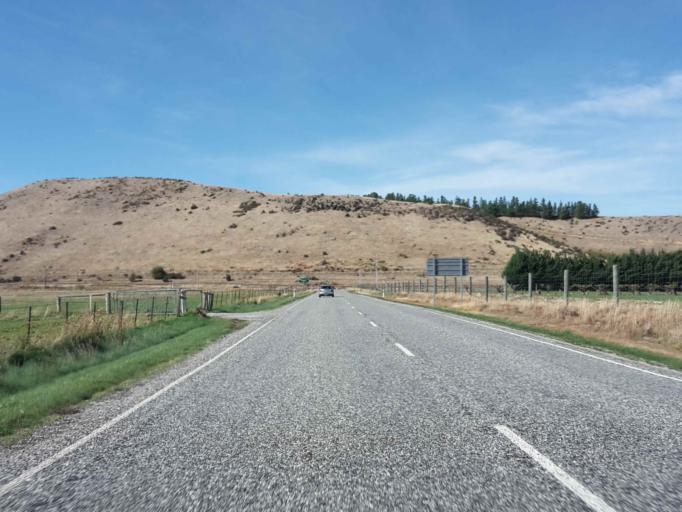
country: NZ
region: Otago
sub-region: Queenstown-Lakes District
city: Wanaka
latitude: -44.8405
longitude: 169.3952
